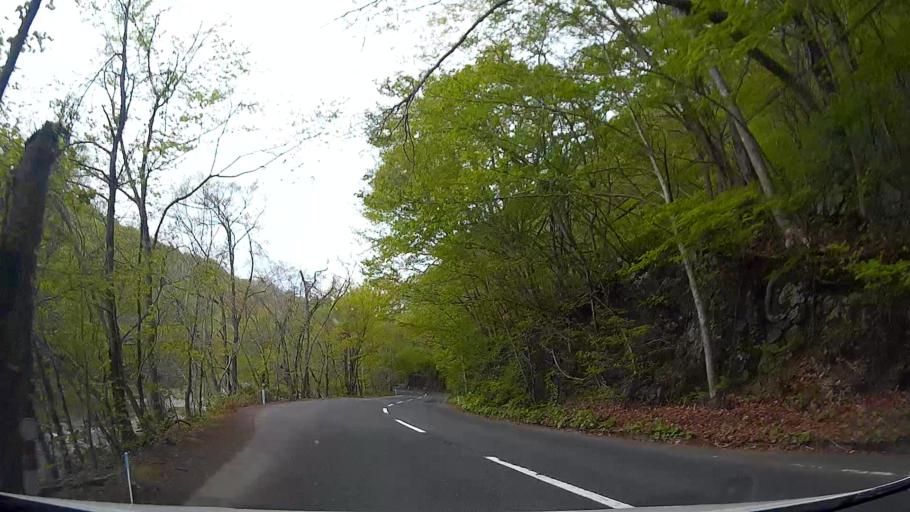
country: JP
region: Aomori
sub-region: Aomori Shi
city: Furudate
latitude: 40.5703
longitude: 140.9792
